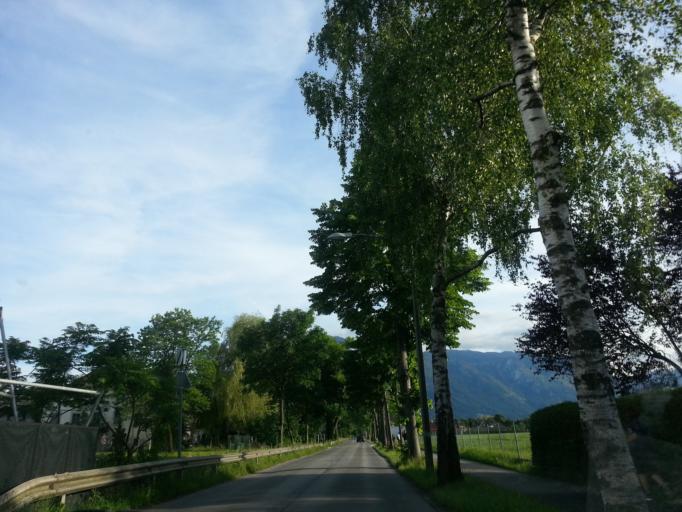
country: AT
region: Salzburg
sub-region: Salzburg Stadt
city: Salzburg
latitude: 47.7884
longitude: 13.0273
